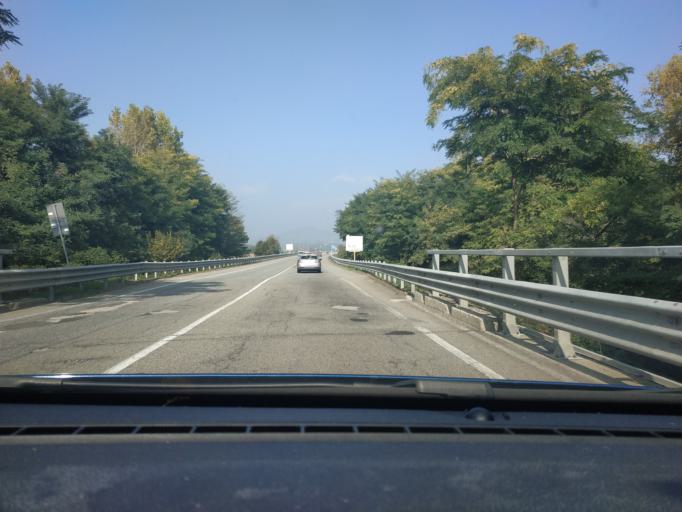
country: IT
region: Piedmont
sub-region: Provincia di Biella
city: Ponderano
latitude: 45.5358
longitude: 8.0400
